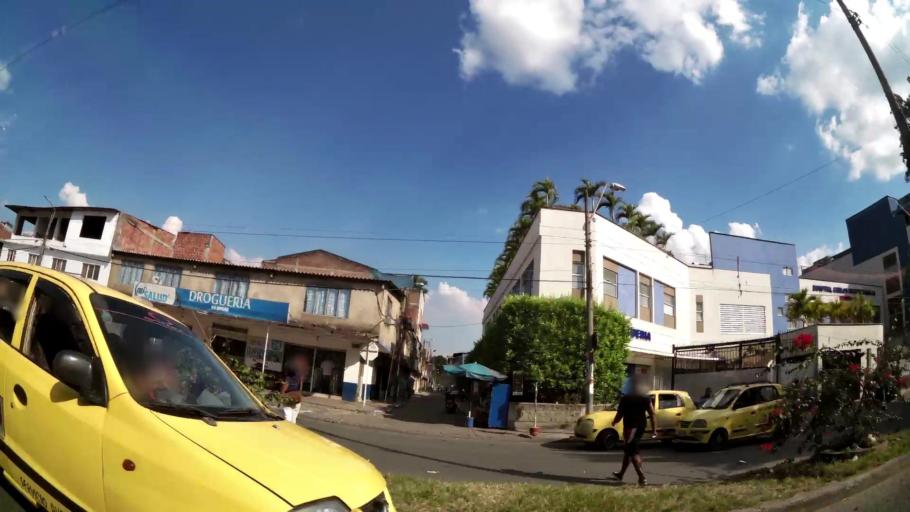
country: CO
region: Valle del Cauca
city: Cali
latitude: 3.4191
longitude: -76.4941
